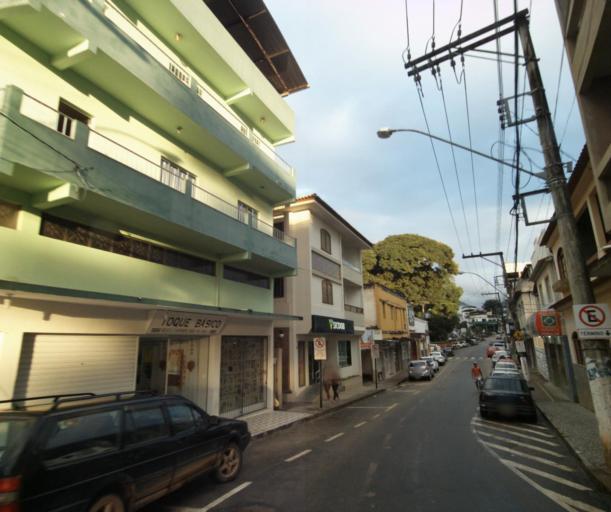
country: BR
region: Espirito Santo
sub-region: Muniz Freire
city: Muniz Freire
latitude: -20.4631
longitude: -41.4146
